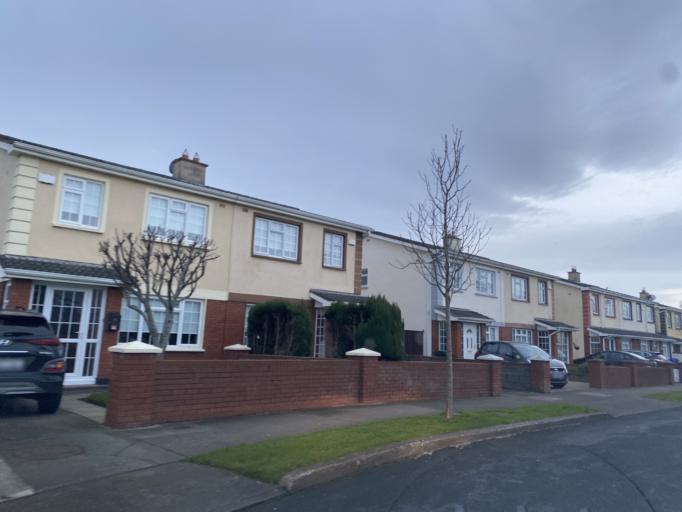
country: IE
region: Leinster
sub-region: Kildare
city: Celbridge
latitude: 53.3478
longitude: -6.5475
